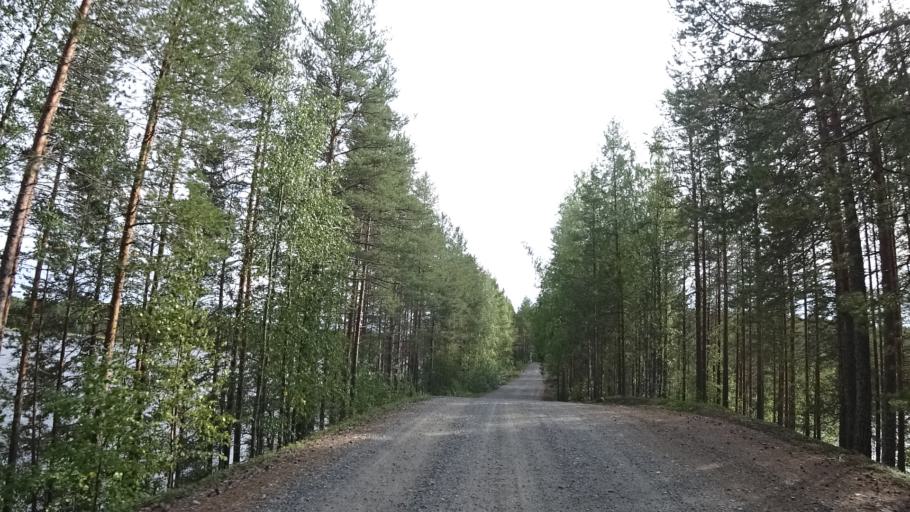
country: FI
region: North Karelia
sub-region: Joensuu
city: Ilomantsi
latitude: 62.6158
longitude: 31.1962
